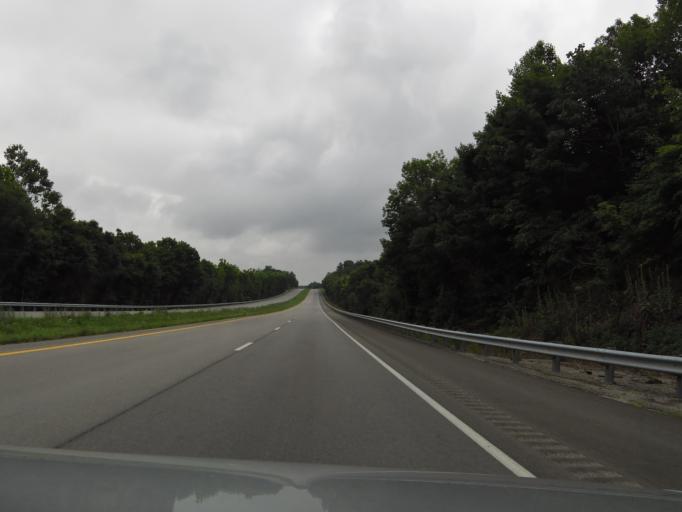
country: US
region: Kentucky
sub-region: Grayson County
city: Leitchfield
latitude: 37.4101
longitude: -86.4777
